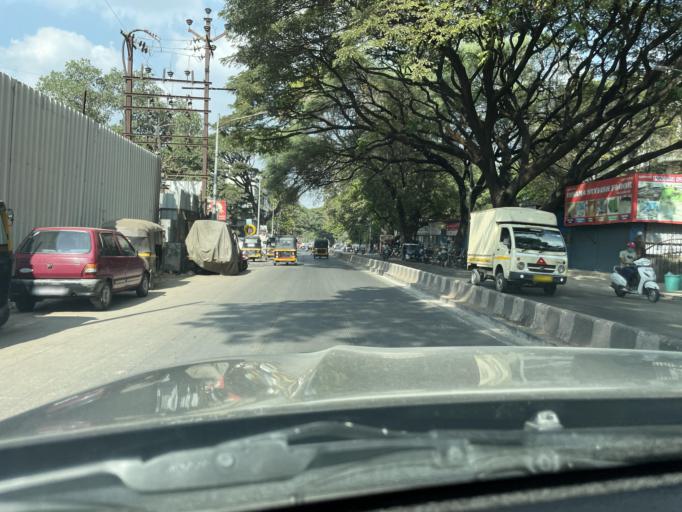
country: IN
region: Maharashtra
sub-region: Pune Division
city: Pune
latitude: 18.4988
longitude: 73.9004
